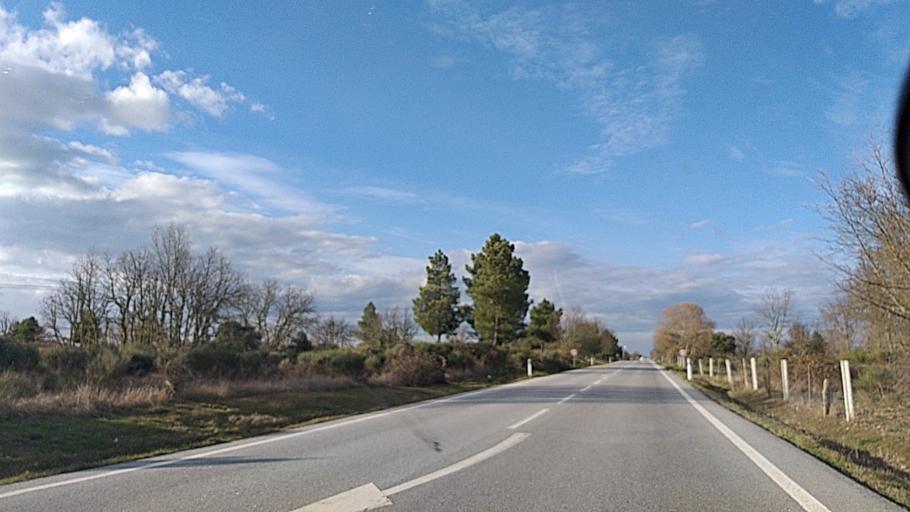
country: ES
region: Castille and Leon
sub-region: Provincia de Salamanca
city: Fuentes de Onoro
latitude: 40.6437
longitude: -6.8562
